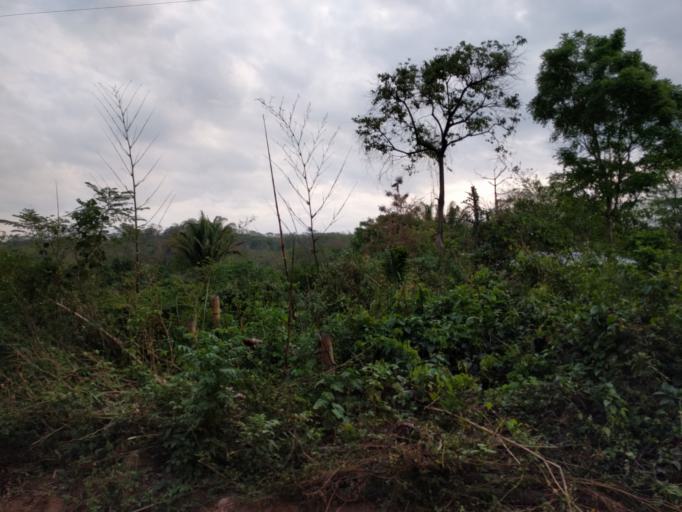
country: BO
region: Santa Cruz
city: Santa Rita
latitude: -17.9295
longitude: -63.3861
